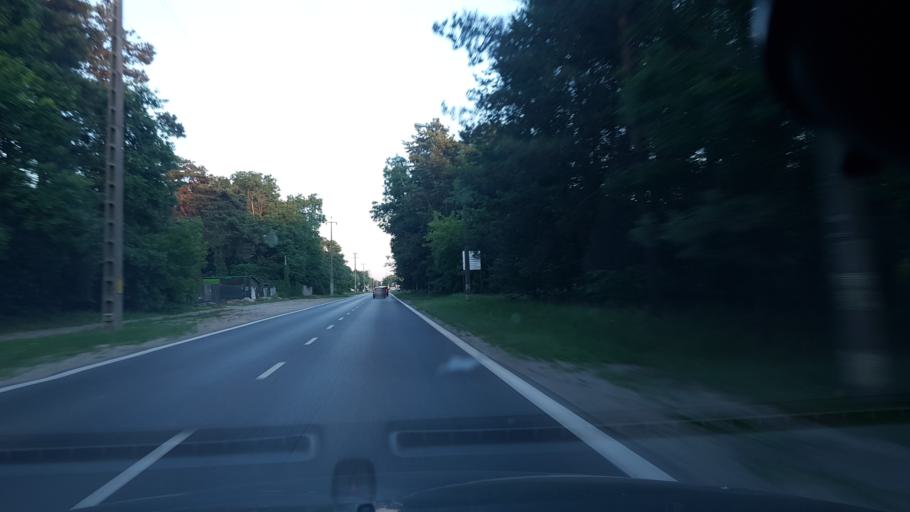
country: PL
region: Masovian Voivodeship
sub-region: Warszawa
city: Wawer
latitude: 52.1763
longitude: 21.1972
